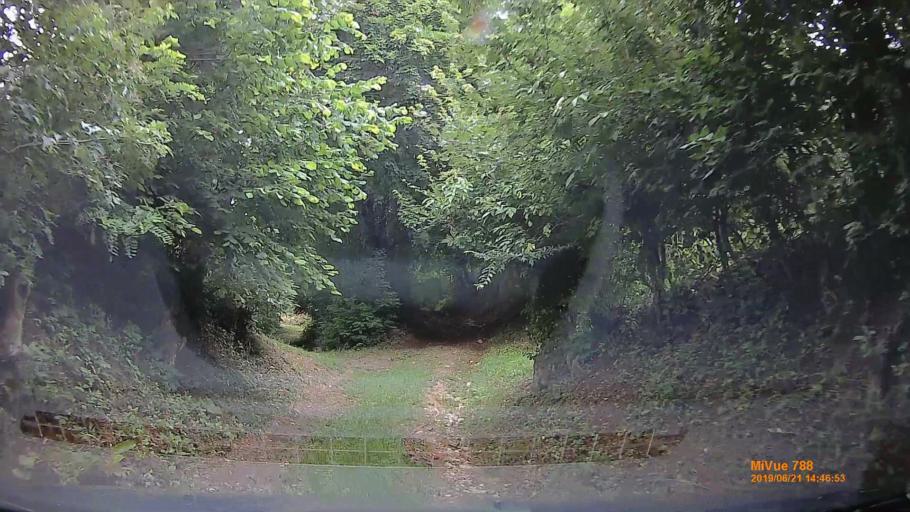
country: HU
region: Baranya
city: Hosszuheteny
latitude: 46.1304
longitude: 18.3090
